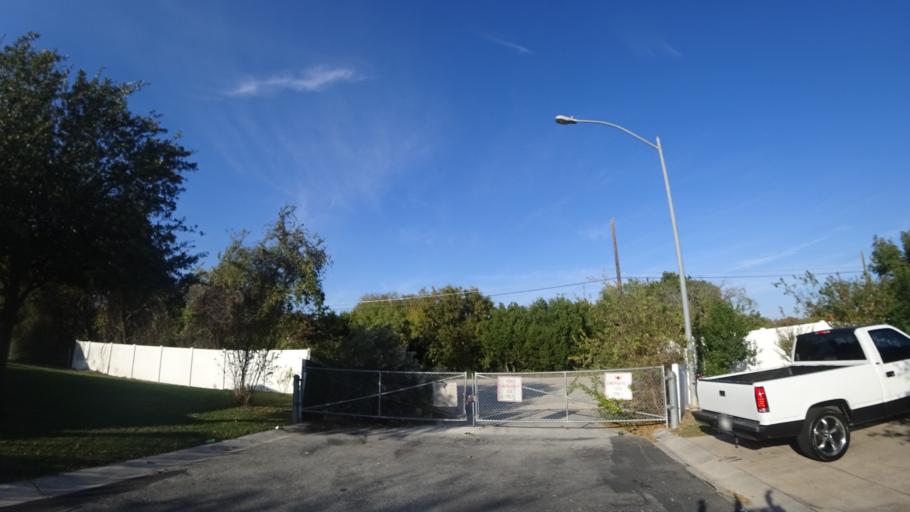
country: US
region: Texas
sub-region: Travis County
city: Pflugerville
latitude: 30.3980
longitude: -97.6366
